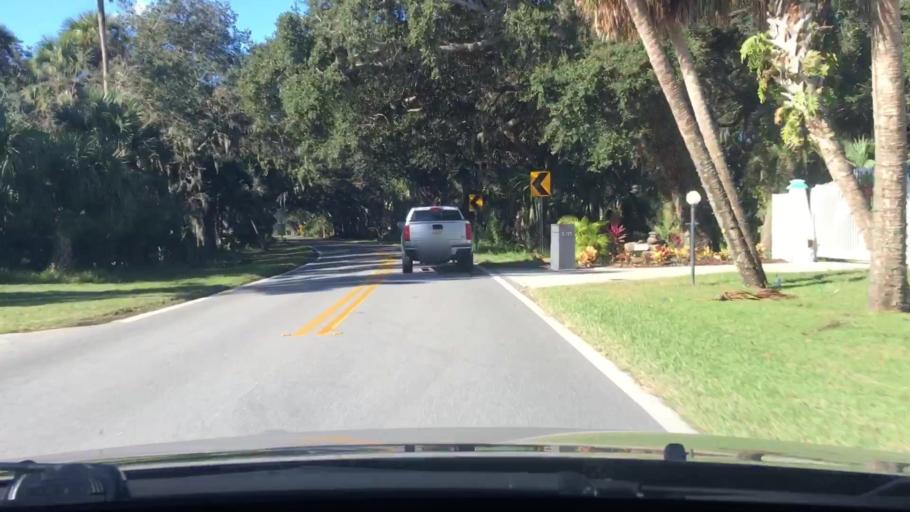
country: US
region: Florida
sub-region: Volusia County
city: Ormond-by-the-Sea
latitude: 29.3469
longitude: -81.0948
